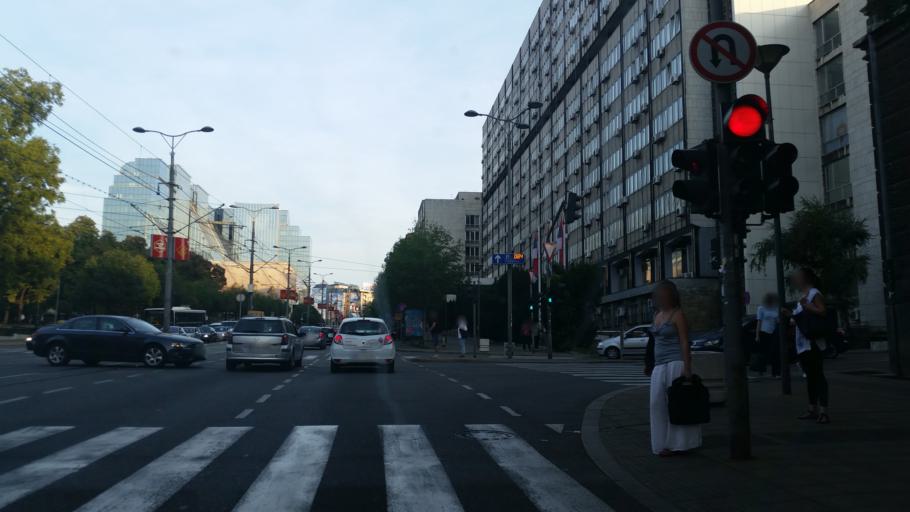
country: RS
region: Central Serbia
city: Belgrade
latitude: 44.8048
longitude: 20.4617
